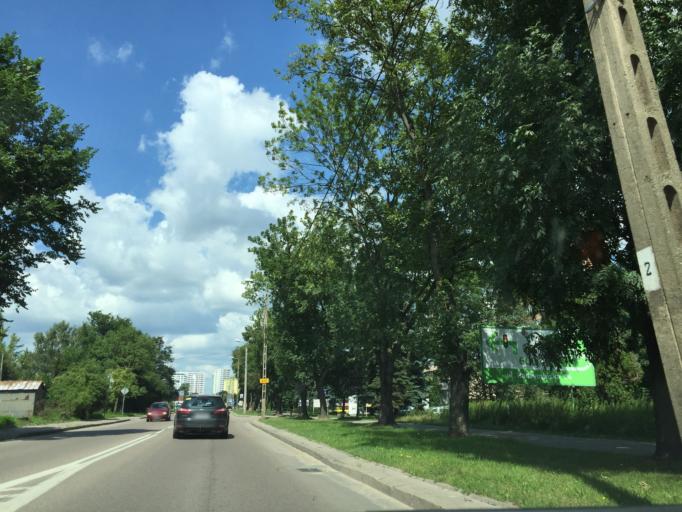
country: PL
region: Podlasie
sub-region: Bialystok
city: Bialystok
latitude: 53.1426
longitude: 23.1578
